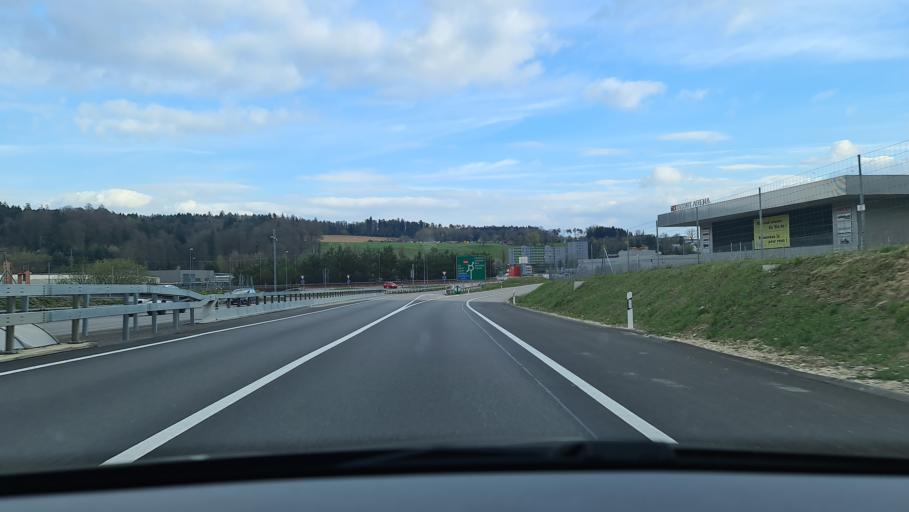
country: CH
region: Bern
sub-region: Biel/Bienne District
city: Orpund
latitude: 47.1588
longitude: 7.2831
